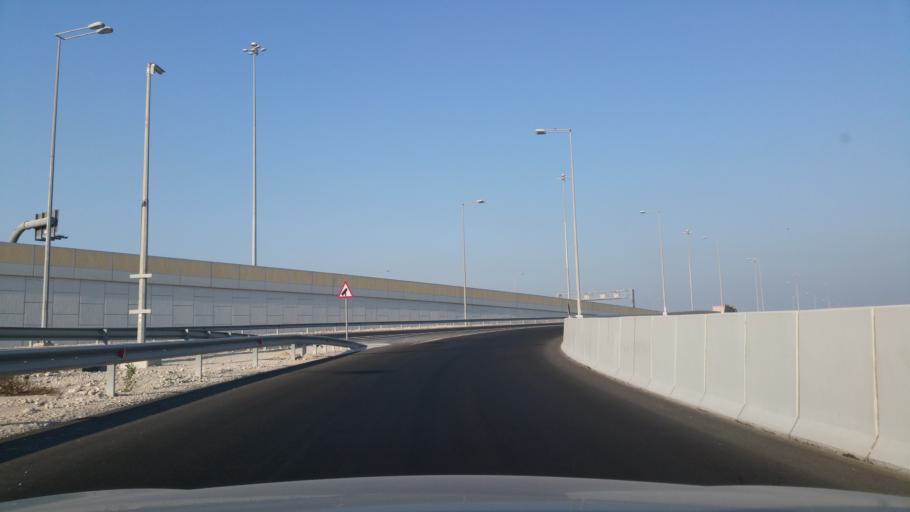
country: QA
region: Al Wakrah
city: Al Wukayr
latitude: 25.1627
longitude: 51.5692
